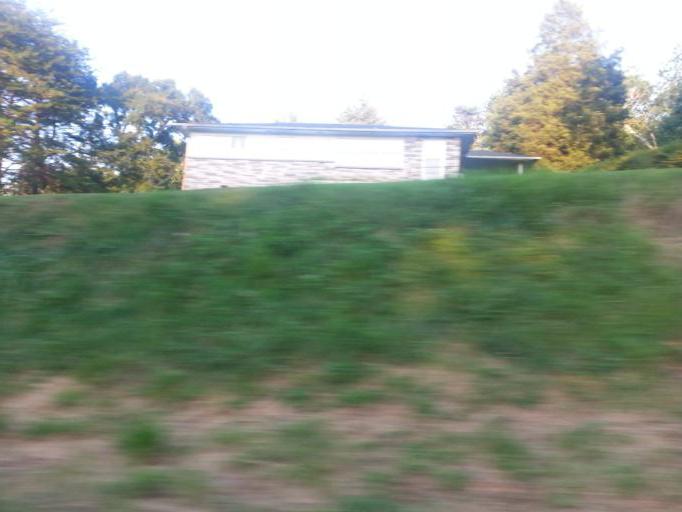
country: US
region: Tennessee
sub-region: Roane County
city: Kingston
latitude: 35.8592
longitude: -84.5261
